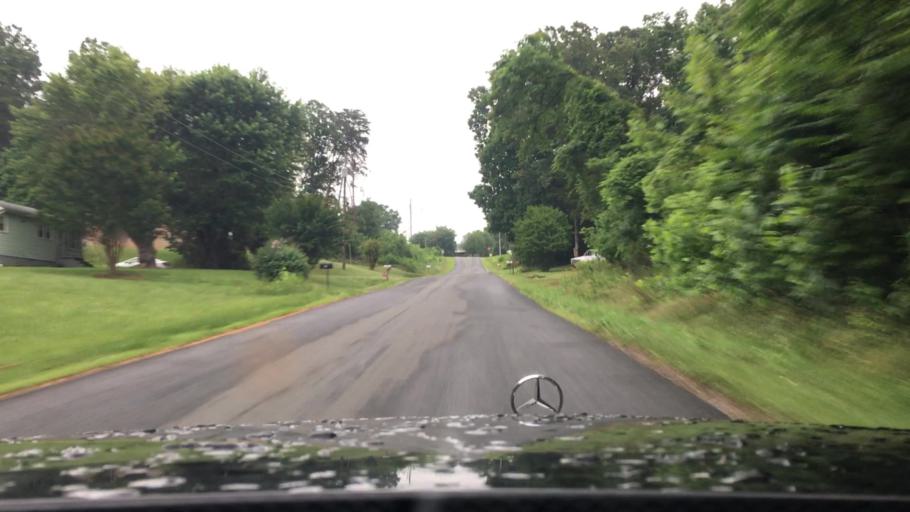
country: US
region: Virginia
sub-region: Pittsylvania County
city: Hurt
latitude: 37.0961
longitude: -79.2974
